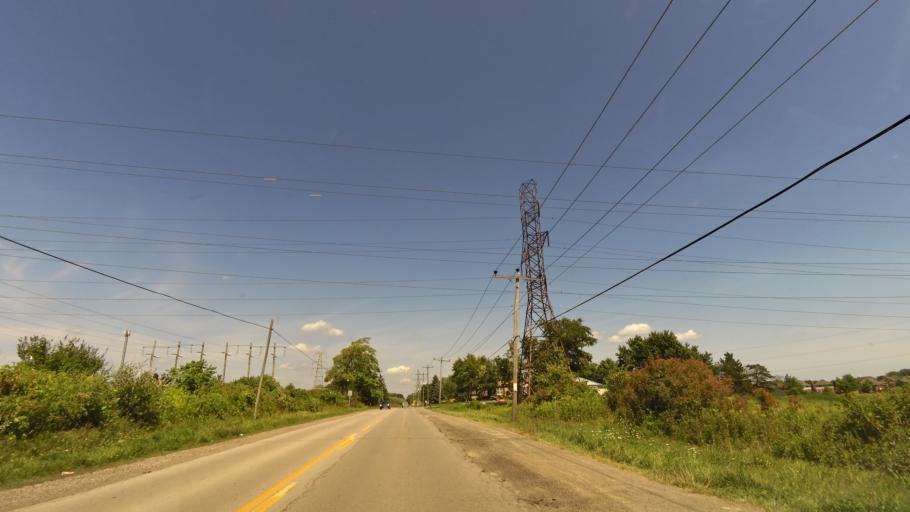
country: CA
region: Ontario
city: Ancaster
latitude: 43.2040
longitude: -79.9303
